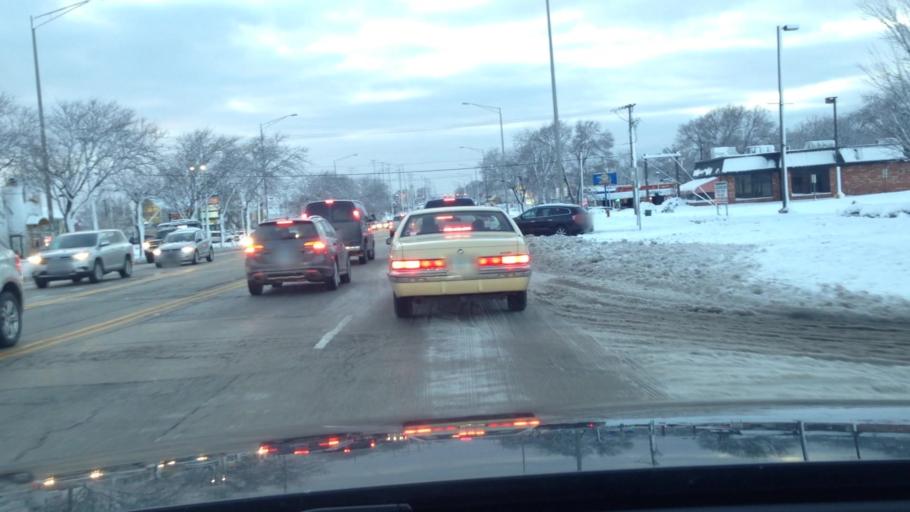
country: US
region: Illinois
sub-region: Cook County
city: Palatine
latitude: 42.1393
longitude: -88.0156
